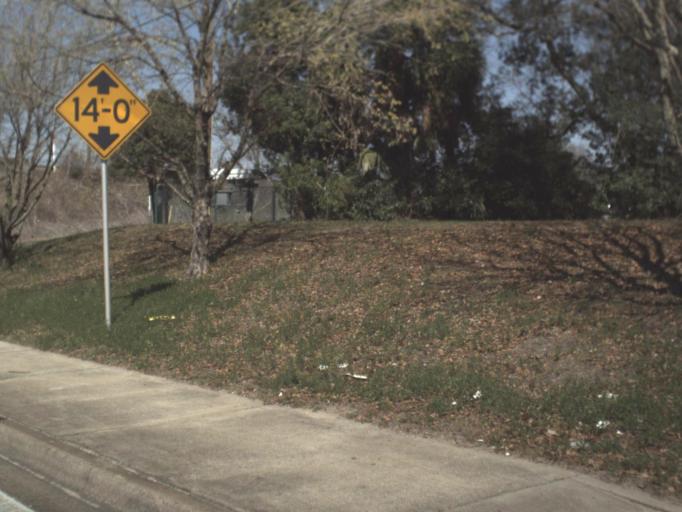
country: US
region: Florida
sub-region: Leon County
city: Tallahassee
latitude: 30.4268
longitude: -84.3022
